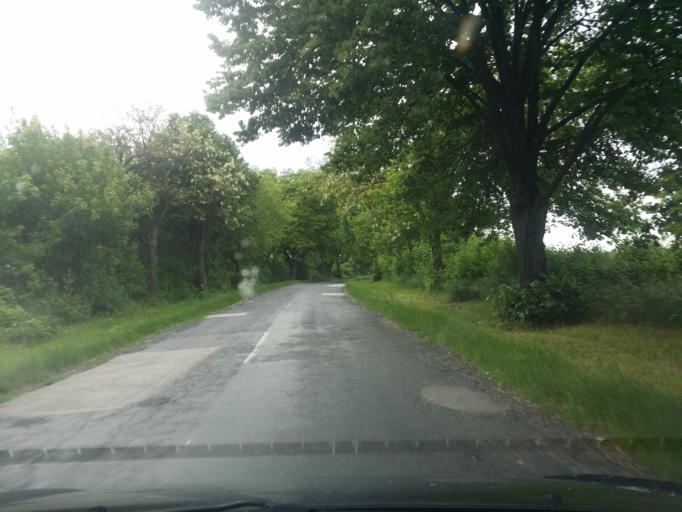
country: HU
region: Somogy
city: Balatonszabadi
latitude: 46.9536
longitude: 18.1715
